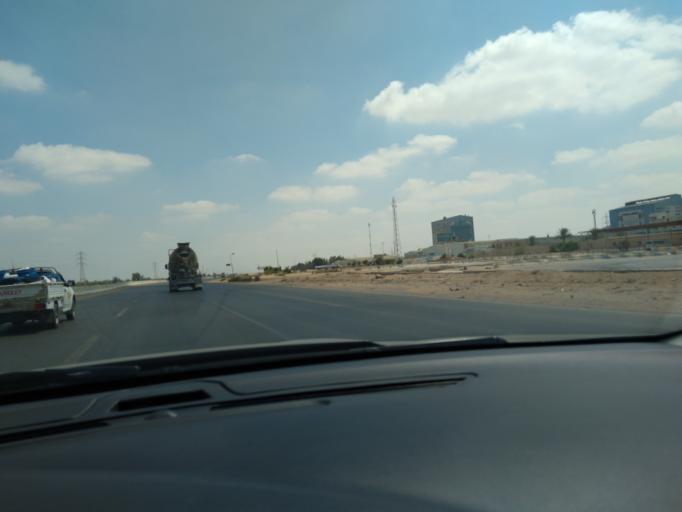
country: EG
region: Al Isma'iliyah
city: At Tall al Kabir
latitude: 30.3418
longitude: 31.8675
